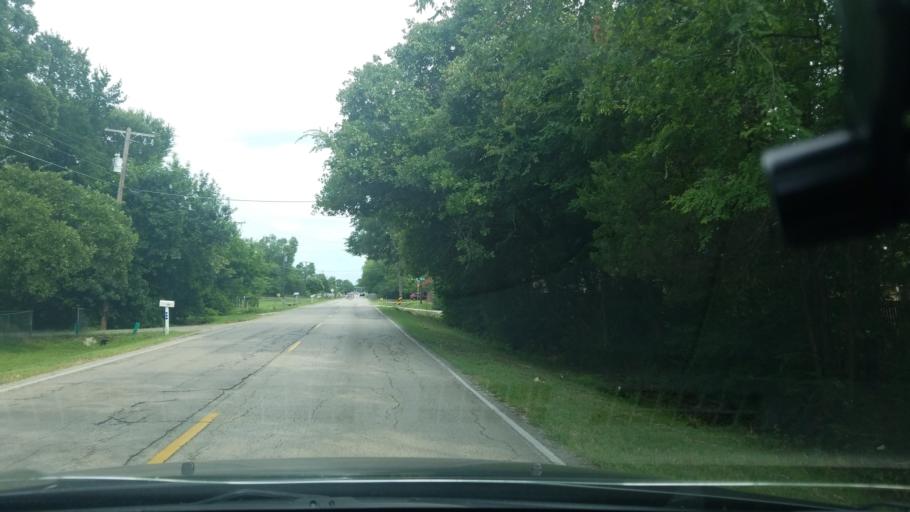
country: US
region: Texas
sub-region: Dallas County
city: Balch Springs
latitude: 32.7537
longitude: -96.6370
